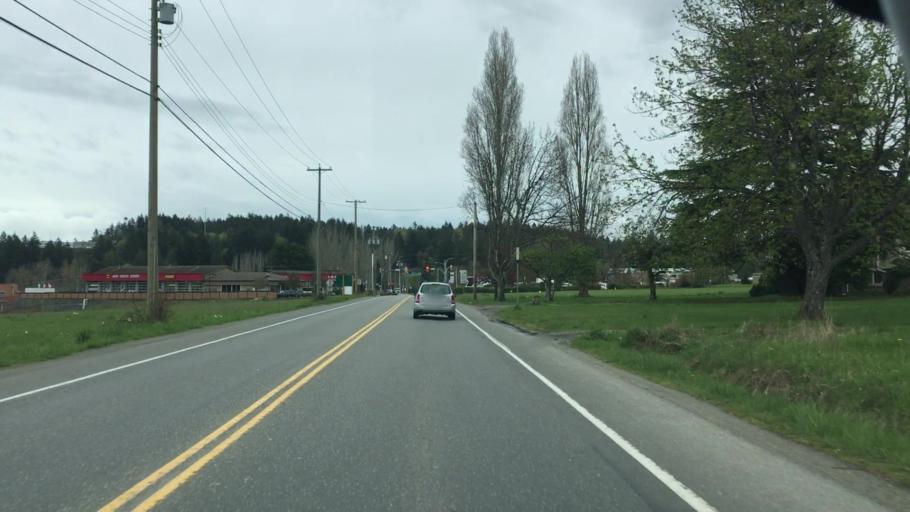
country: CA
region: British Columbia
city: North Saanich
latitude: 48.5671
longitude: -123.4402
